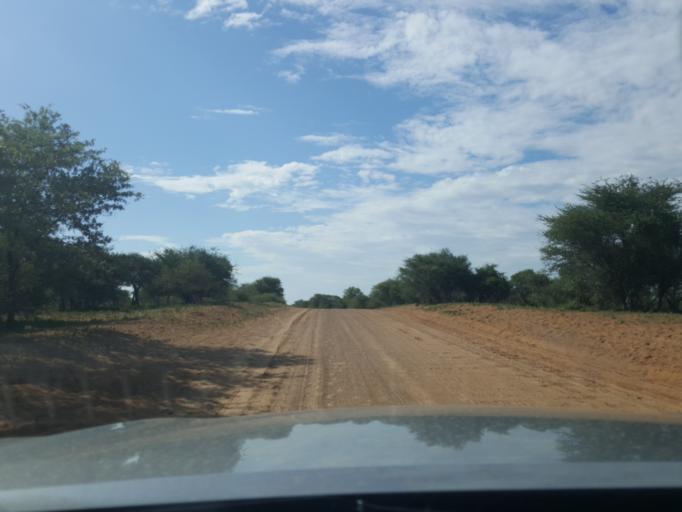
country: BW
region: Kweneng
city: Khudumelapye
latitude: -23.5405
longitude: 24.7290
